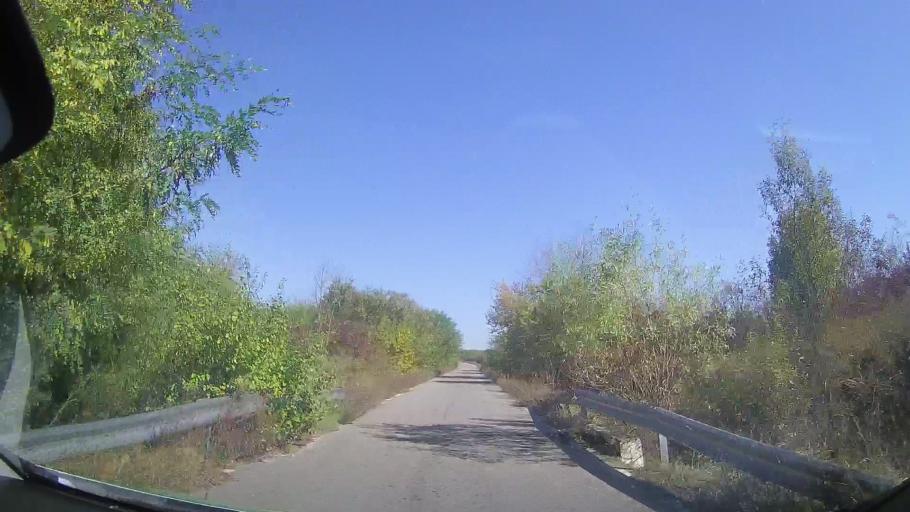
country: RO
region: Timis
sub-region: Comuna Ohaba Lunga
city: Ohaba Lunga
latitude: 45.9159
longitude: 21.9534
